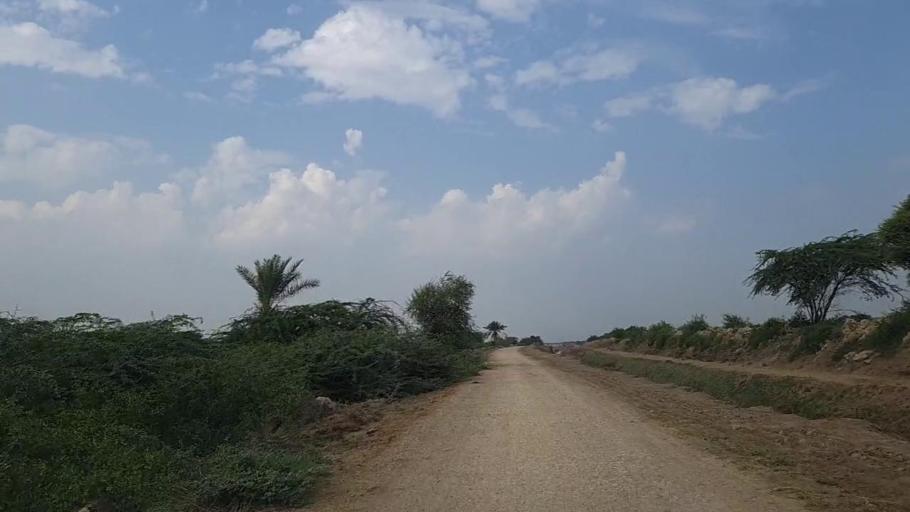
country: PK
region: Sindh
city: Daro Mehar
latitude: 24.7180
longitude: 68.1395
